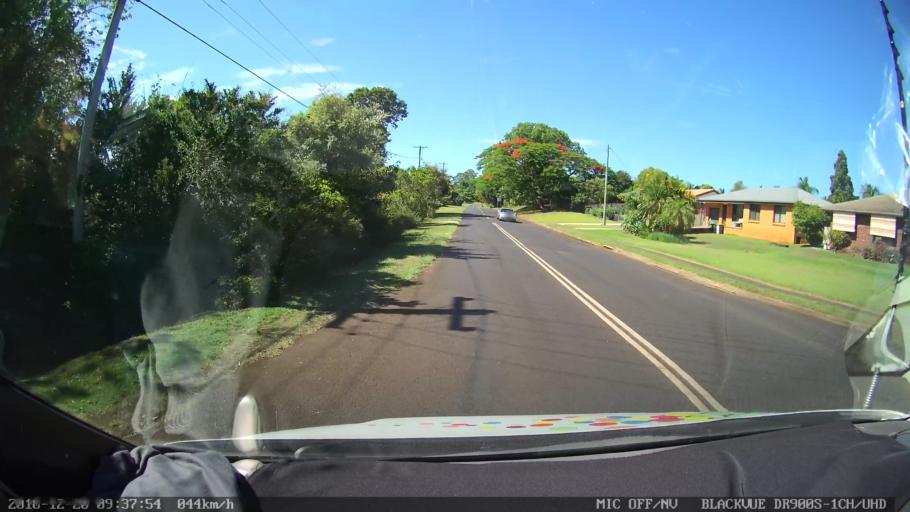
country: AU
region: New South Wales
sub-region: Lismore Municipality
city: Nimbin
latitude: -28.6869
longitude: 153.3148
